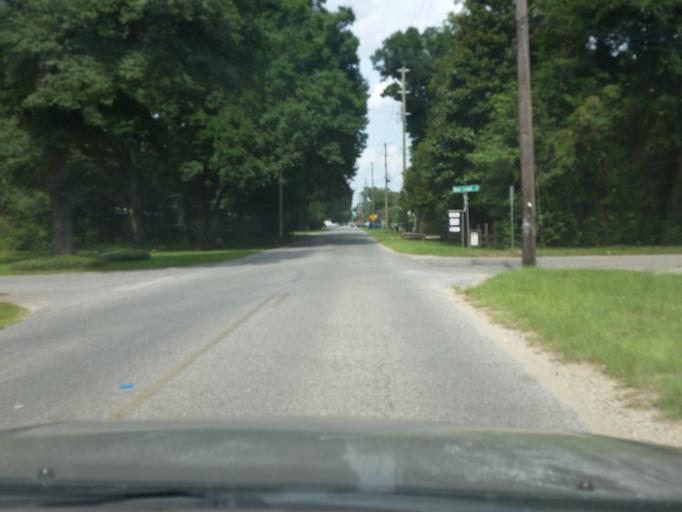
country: US
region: Florida
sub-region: Escambia County
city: Brent
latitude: 30.4650
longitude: -87.2565
